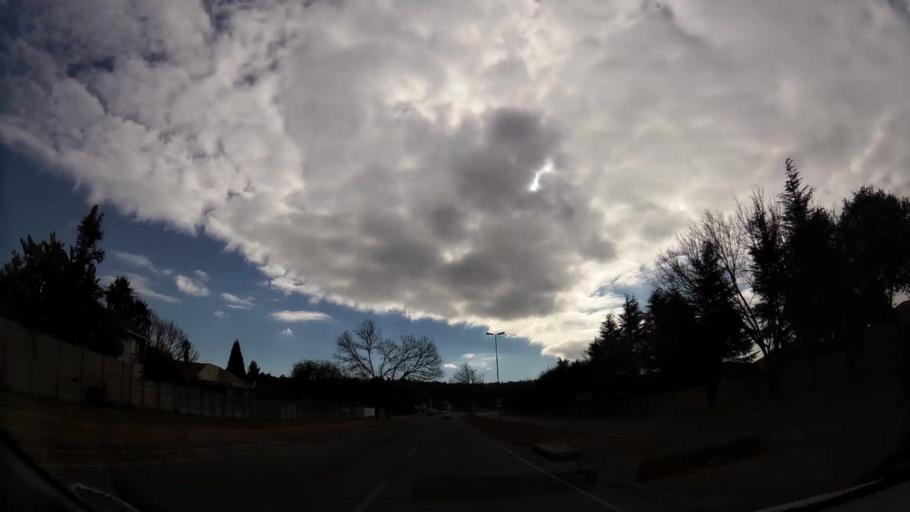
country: ZA
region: Gauteng
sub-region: City of Johannesburg Metropolitan Municipality
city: Roodepoort
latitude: -26.1107
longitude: 27.8546
